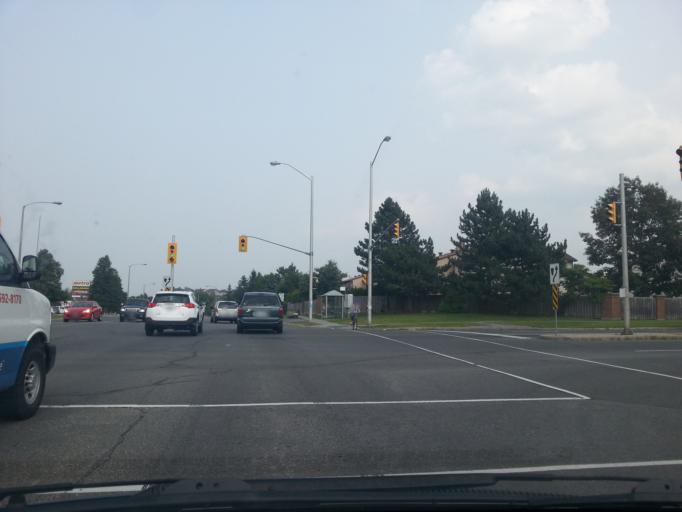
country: CA
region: Quebec
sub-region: Outaouais
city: Gatineau
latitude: 45.4787
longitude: -75.5380
